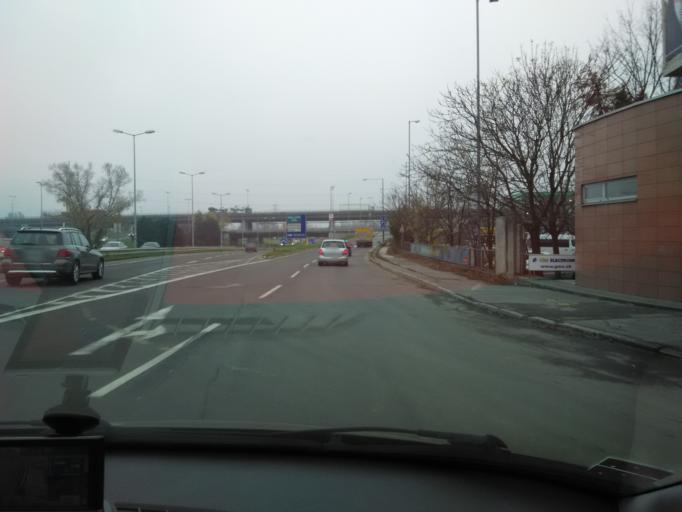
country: SK
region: Bratislavsky
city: Bratislava
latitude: 48.1444
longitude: 17.1514
